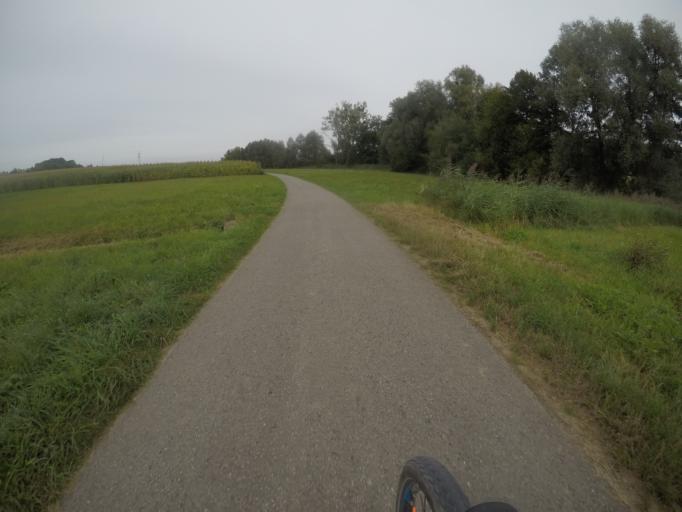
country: DE
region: Baden-Wuerttemberg
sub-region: Regierungsbezirk Stuttgart
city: Magstadt
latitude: 48.7427
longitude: 8.9843
